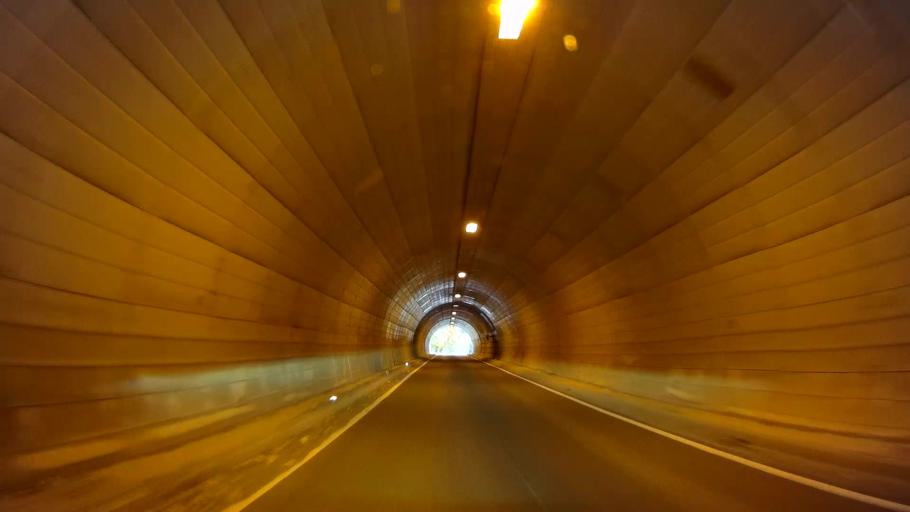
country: JP
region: Gunma
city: Nakanojomachi
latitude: 36.6499
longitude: 138.6508
